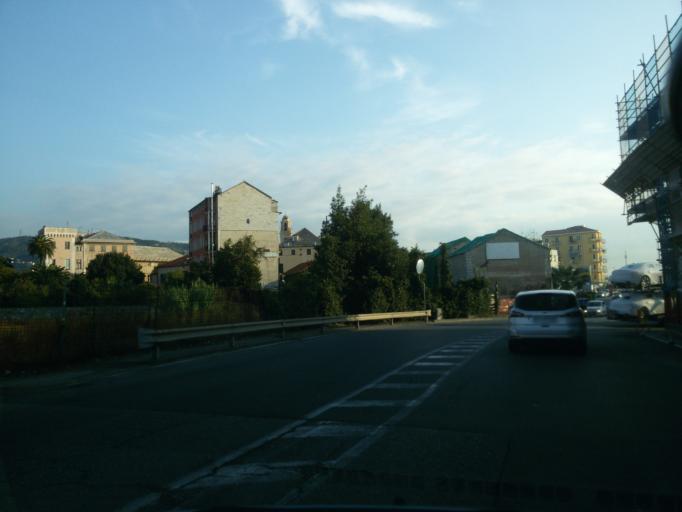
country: IT
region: Liguria
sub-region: Provincia di Savona
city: Valleggia
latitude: 44.2935
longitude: 8.4519
